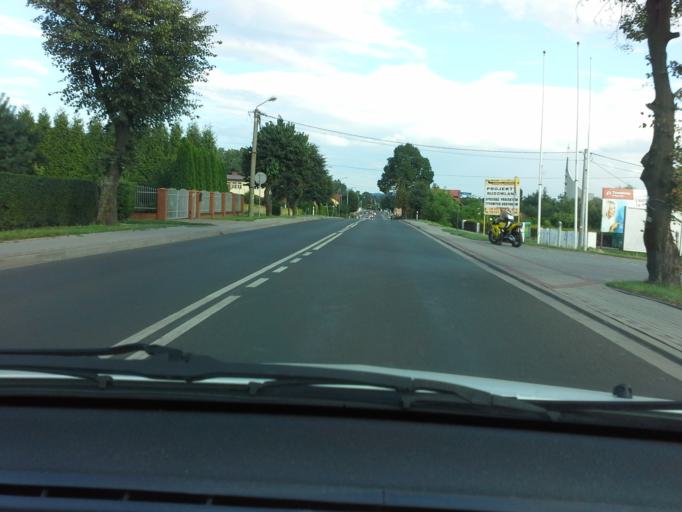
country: PL
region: Lesser Poland Voivodeship
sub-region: Powiat chrzanowski
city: Trzebinia
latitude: 50.1525
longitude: 19.4868
